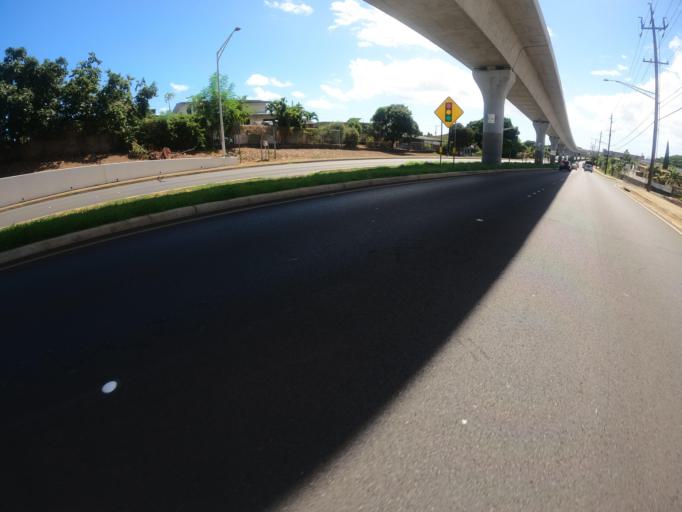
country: US
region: Hawaii
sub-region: Honolulu County
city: Waipahu
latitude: 21.3877
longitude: -157.9966
